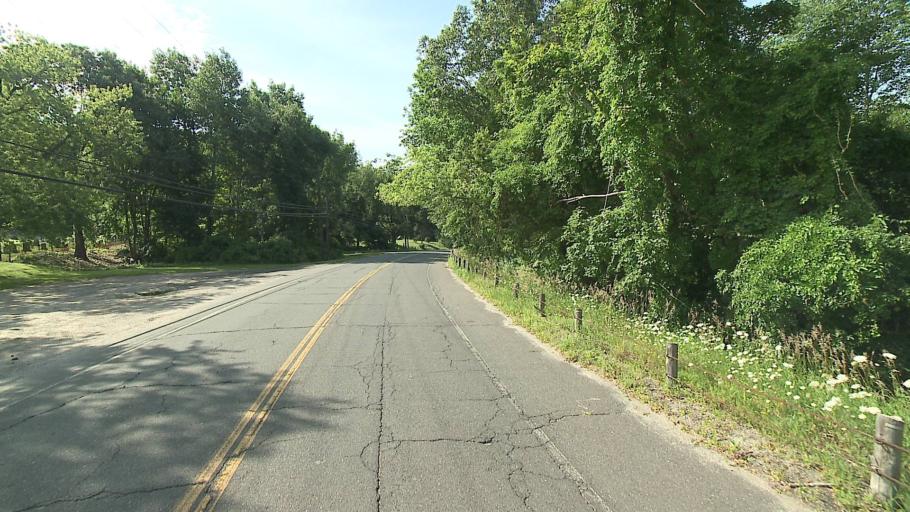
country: US
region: New York
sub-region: Putnam County
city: Putnam Lake
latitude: 41.4803
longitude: -73.4966
